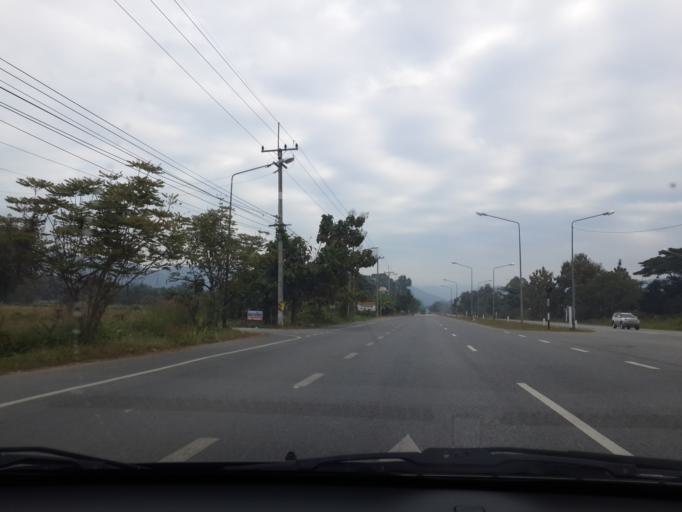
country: TH
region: Chiang Mai
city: San Sai
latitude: 18.8806
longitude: 99.1467
